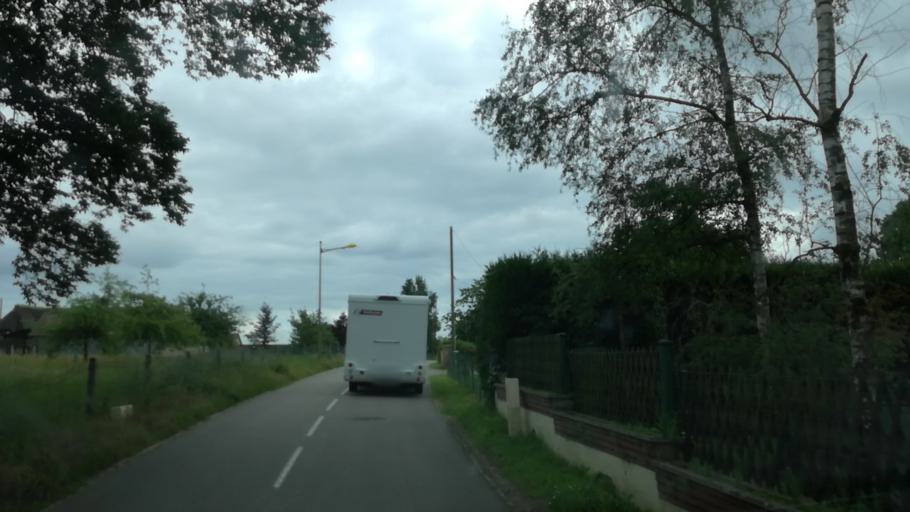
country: FR
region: Haute-Normandie
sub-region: Departement de l'Eure
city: Bourg-Achard
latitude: 49.3331
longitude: 0.8119
